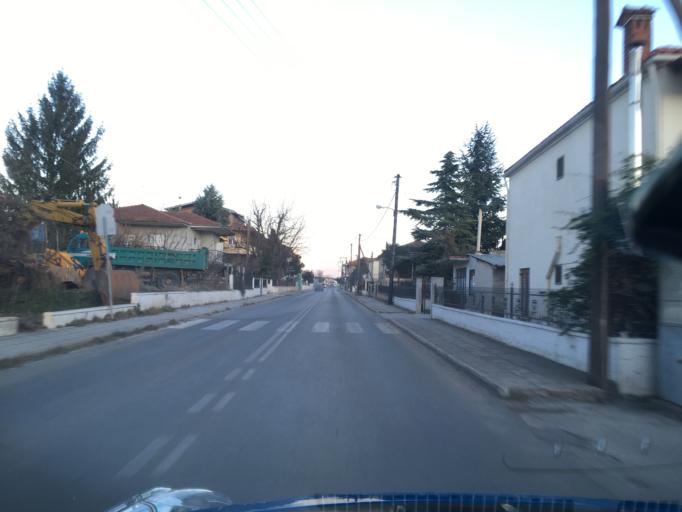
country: GR
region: West Macedonia
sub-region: Nomos Kozanis
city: Kozani
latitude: 40.2707
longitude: 21.7779
